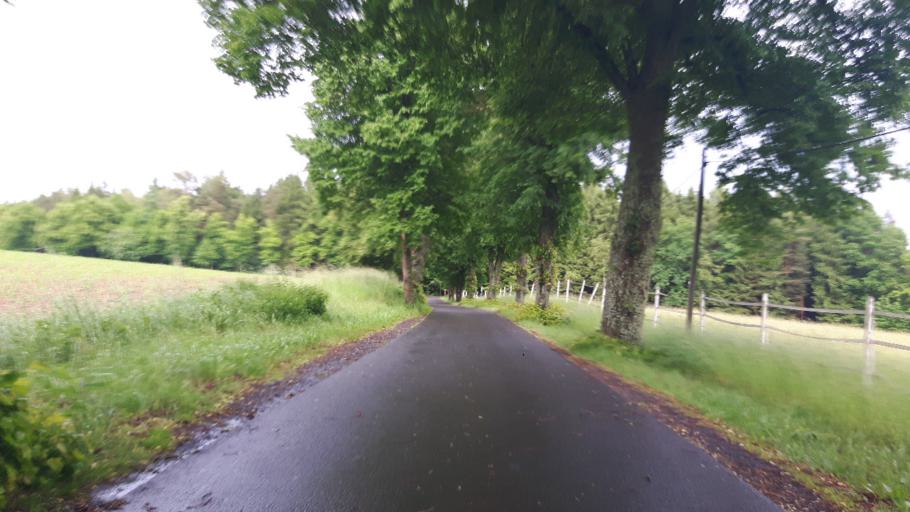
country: DE
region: Thuringia
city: Bockstadt
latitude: 50.4062
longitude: 10.8929
